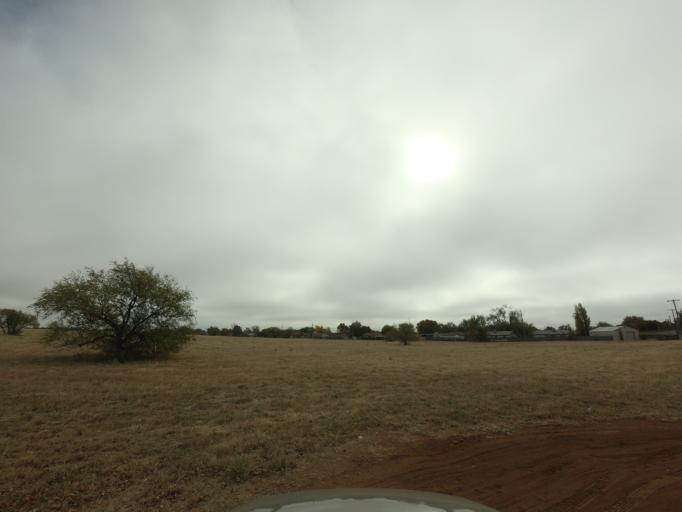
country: US
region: New Mexico
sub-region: Curry County
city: Clovis
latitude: 34.4328
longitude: -103.2228
